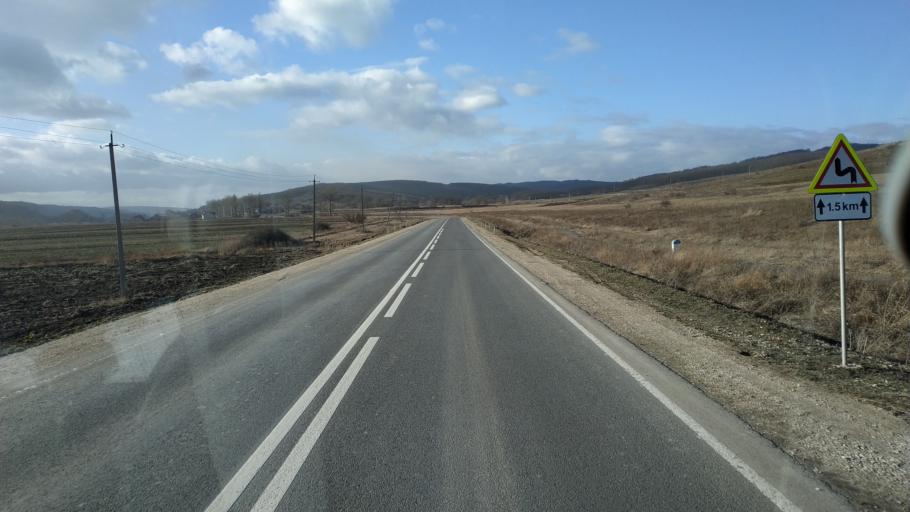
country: MD
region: Calarasi
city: Calarasi
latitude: 47.3251
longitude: 28.1031
